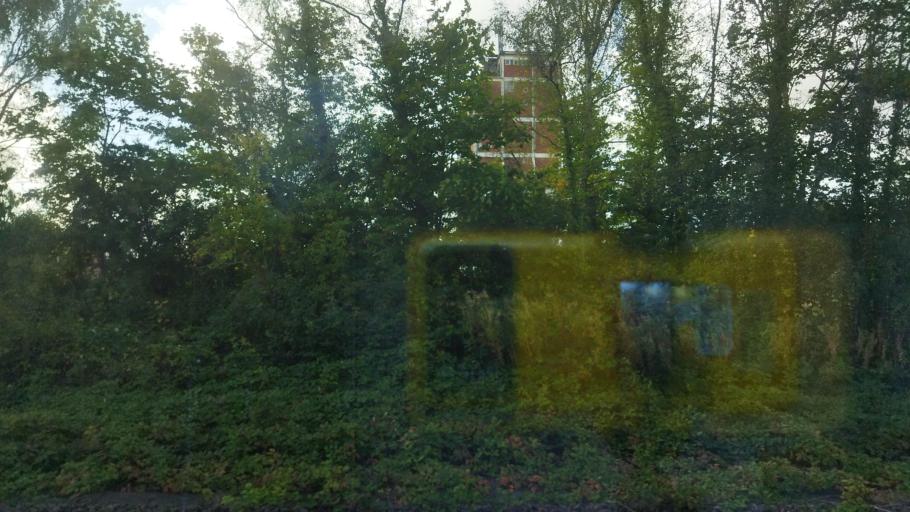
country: DE
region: Lower Saxony
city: Emden
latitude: 53.3635
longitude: 7.1980
